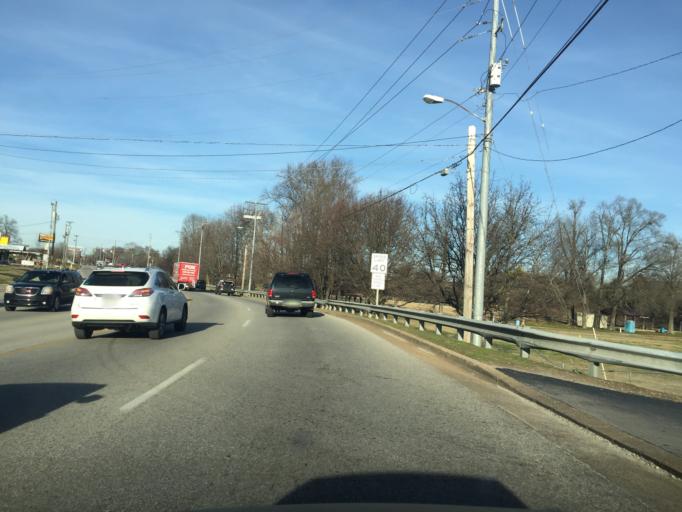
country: US
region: Tennessee
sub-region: Hamilton County
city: Red Bank
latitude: 35.1153
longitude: -85.2518
